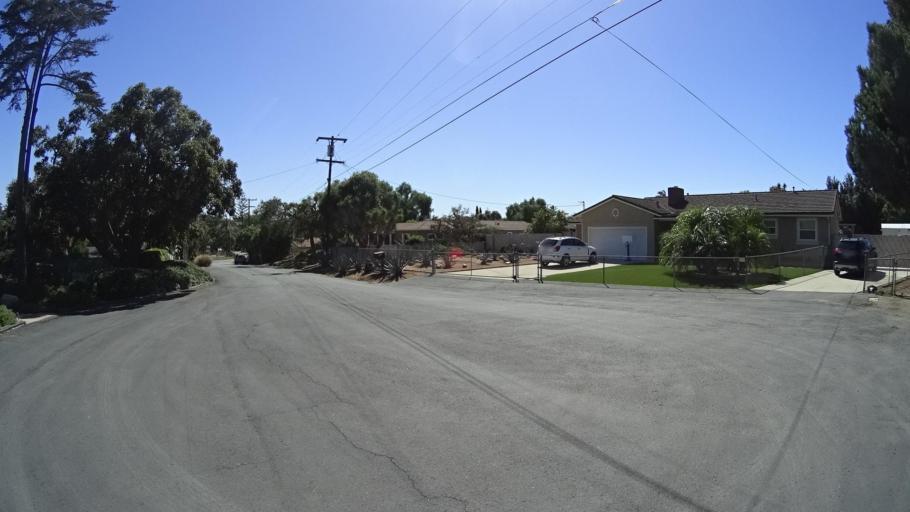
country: US
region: California
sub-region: San Diego County
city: Bonita
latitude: 32.6544
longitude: -117.0554
